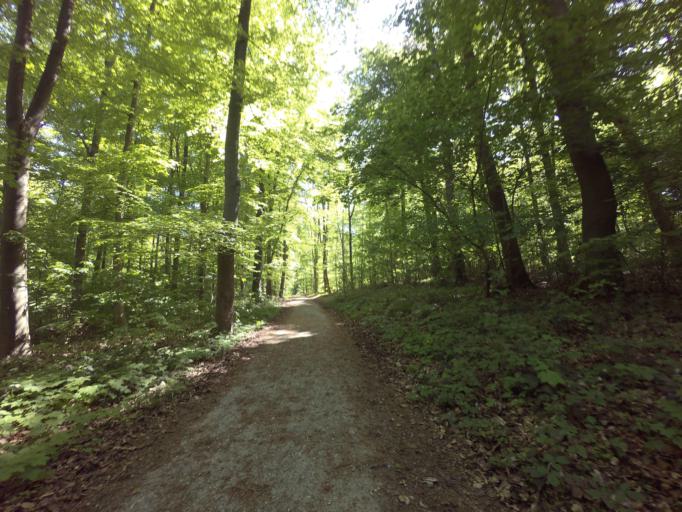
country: DE
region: Lower Saxony
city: Hildesheim
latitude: 52.1379
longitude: 9.9895
